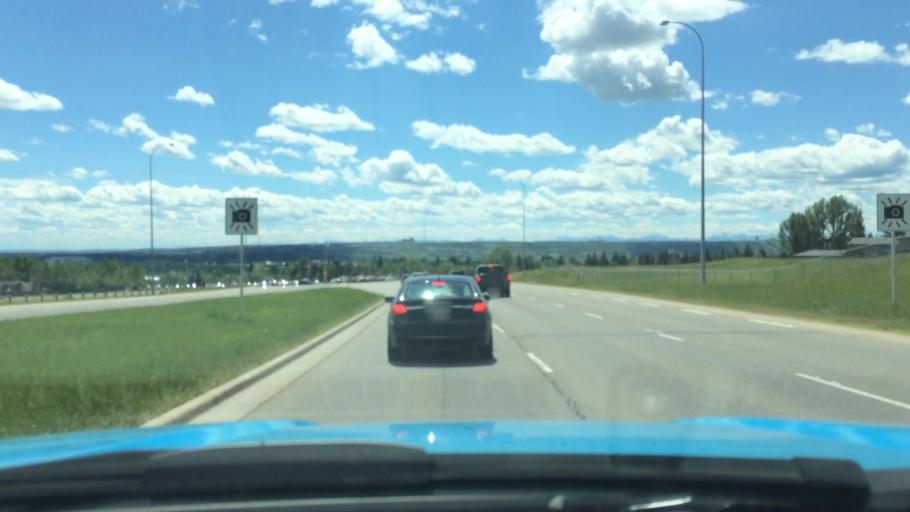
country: CA
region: Alberta
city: Calgary
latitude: 51.1115
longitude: -114.1382
